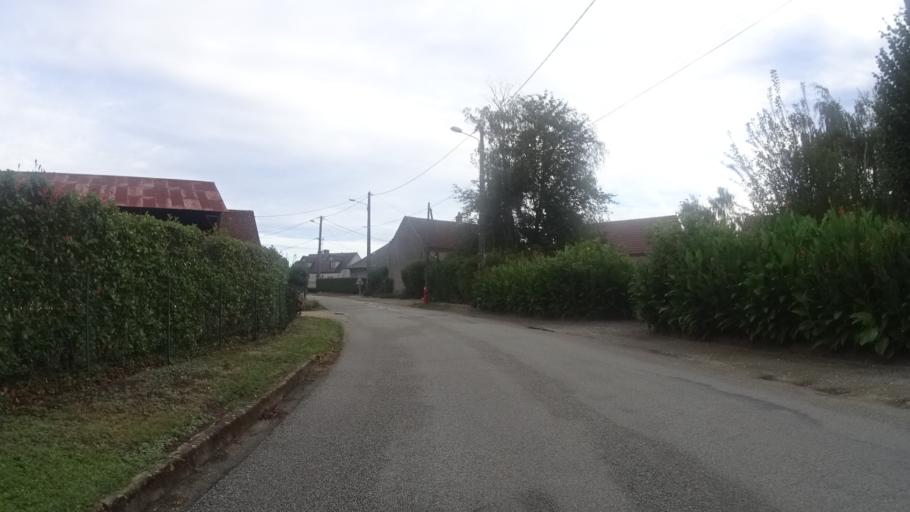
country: FR
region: Centre
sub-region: Departement du Loiret
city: Saint-Benoit-sur-Loire
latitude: 47.8037
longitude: 2.3130
